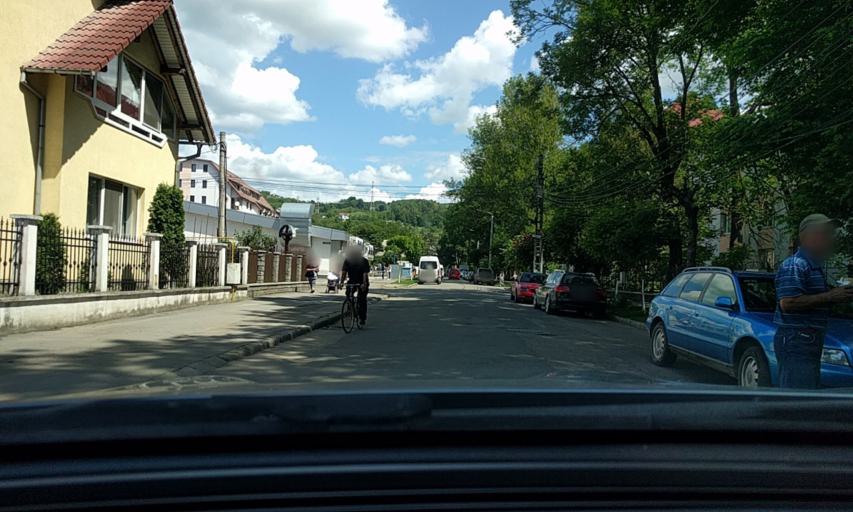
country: RO
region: Bistrita-Nasaud
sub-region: Oras Nasaud
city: Nasaud
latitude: 47.2818
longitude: 24.4093
